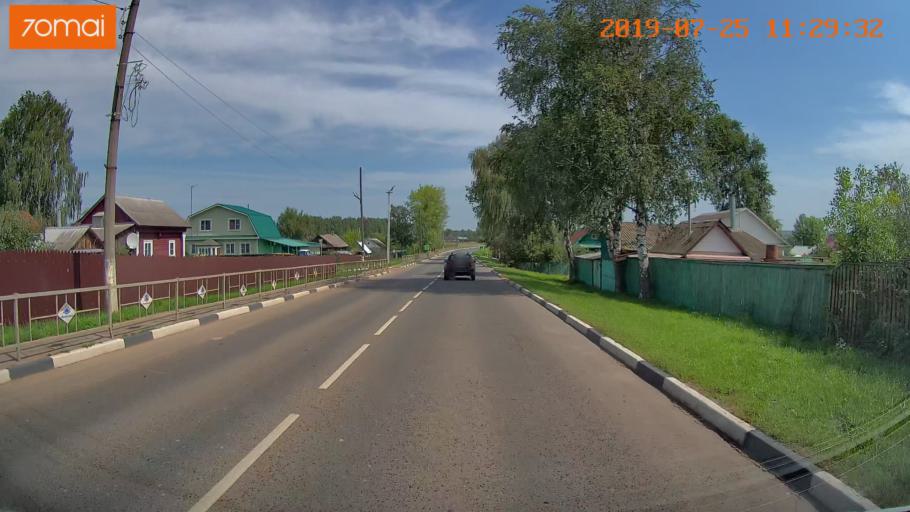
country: RU
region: Ivanovo
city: Privolzhsk
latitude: 57.3852
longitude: 41.3072
